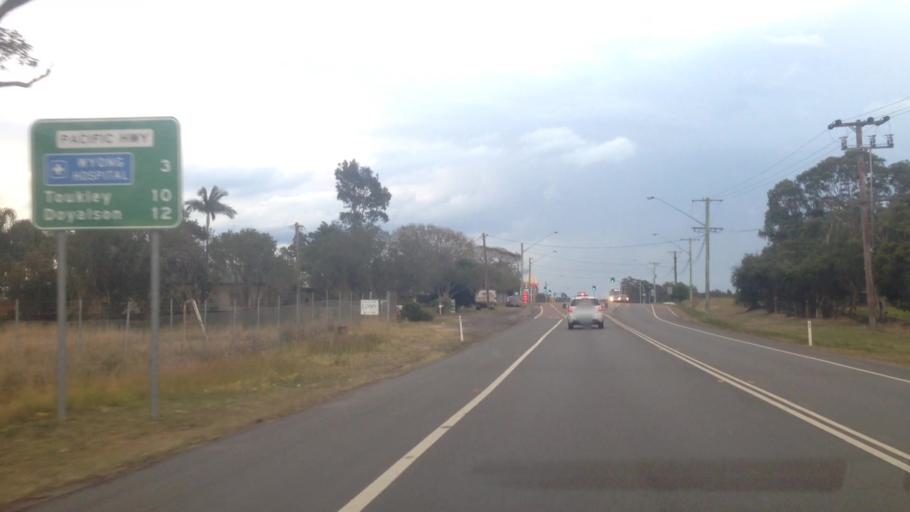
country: AU
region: New South Wales
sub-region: Wyong Shire
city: Tuggerawong
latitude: -33.2676
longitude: 151.4545
